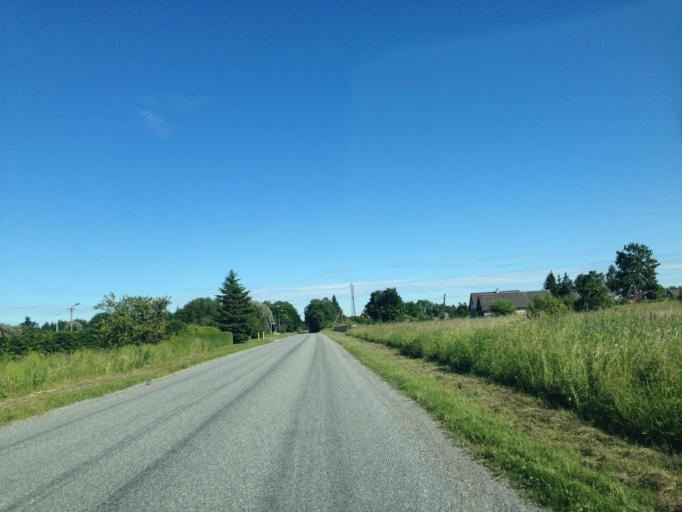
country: EE
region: Harju
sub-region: Raasiku vald
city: Raasiku
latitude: 59.4410
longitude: 25.1388
